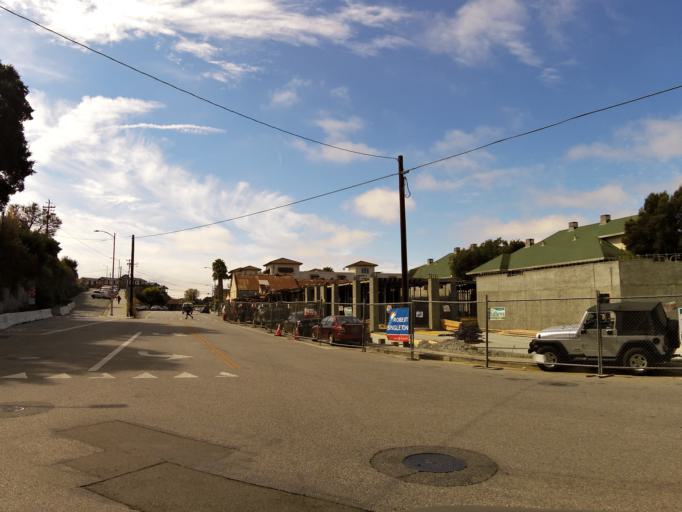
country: US
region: California
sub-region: Santa Cruz County
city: Santa Cruz
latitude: 36.9668
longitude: -122.0243
